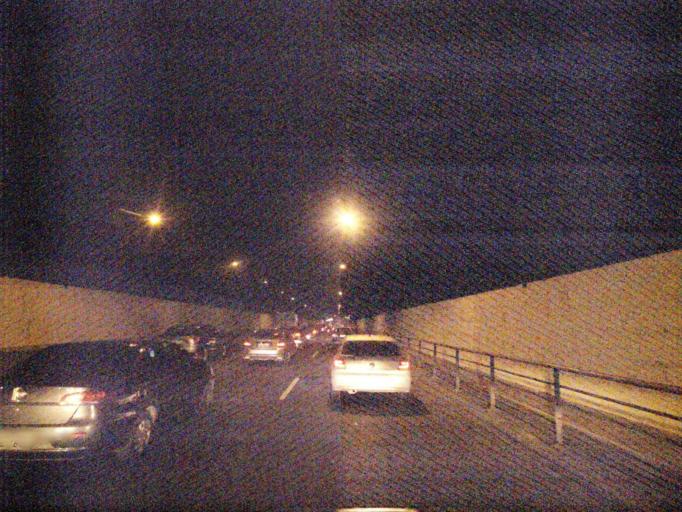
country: BR
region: Rio de Janeiro
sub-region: Niteroi
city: Niteroi
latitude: -22.9118
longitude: -43.0984
